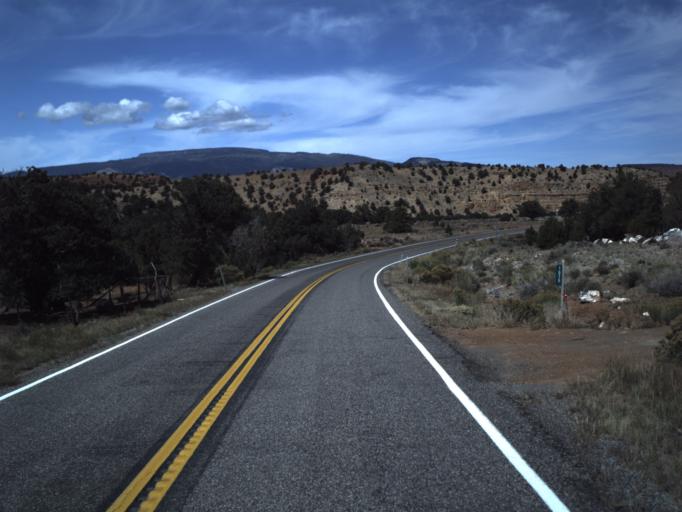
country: US
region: Utah
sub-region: Wayne County
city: Loa
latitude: 38.2516
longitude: -111.3786
